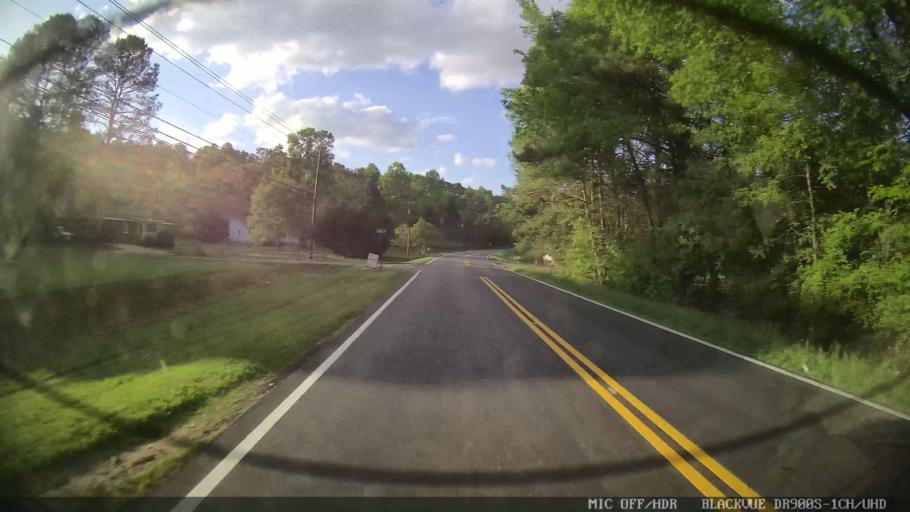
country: US
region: Georgia
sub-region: Bartow County
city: Cartersville
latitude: 34.2430
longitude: -84.8101
